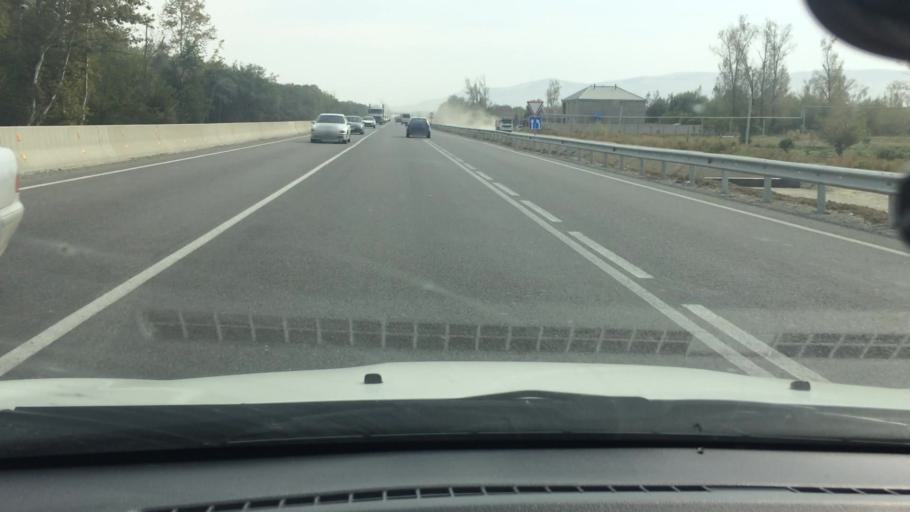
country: GE
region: Kvemo Kartli
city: Rust'avi
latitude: 41.6249
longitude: 44.9246
